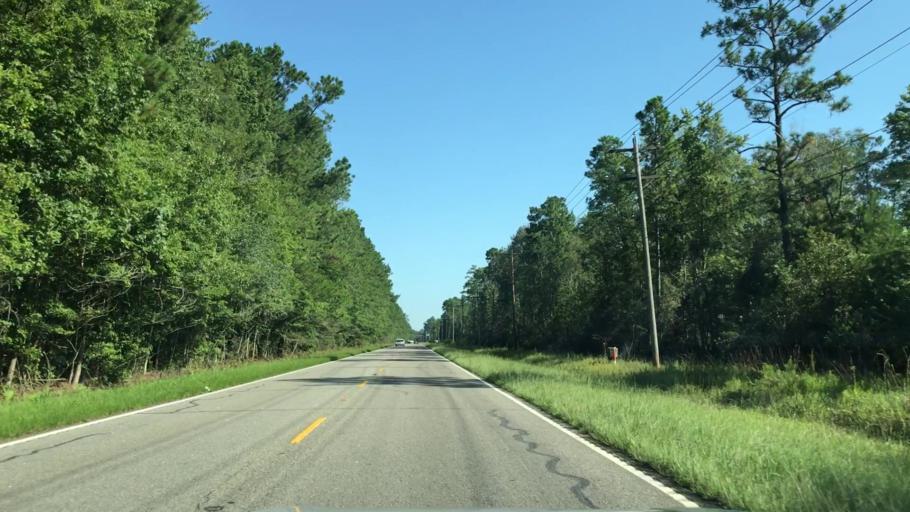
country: US
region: South Carolina
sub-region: Georgetown County
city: Georgetown
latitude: 33.4458
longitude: -79.2781
